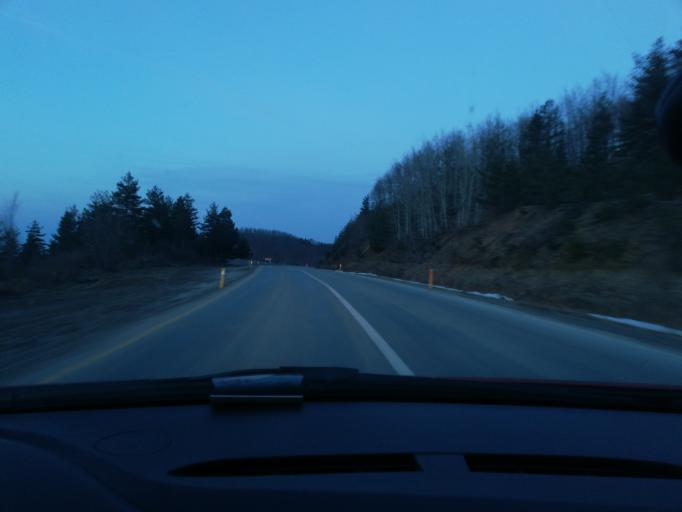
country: TR
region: Kastamonu
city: Inebolu
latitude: 41.9004
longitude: 33.7190
